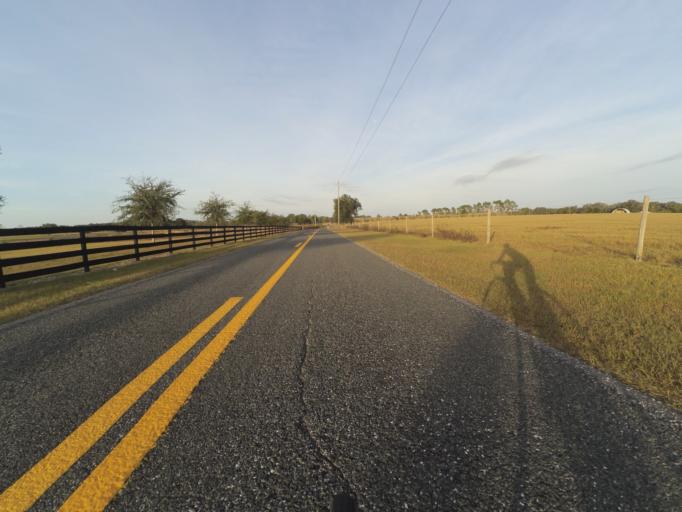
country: US
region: Florida
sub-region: Lake County
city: Umatilla
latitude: 28.9456
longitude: -81.6971
